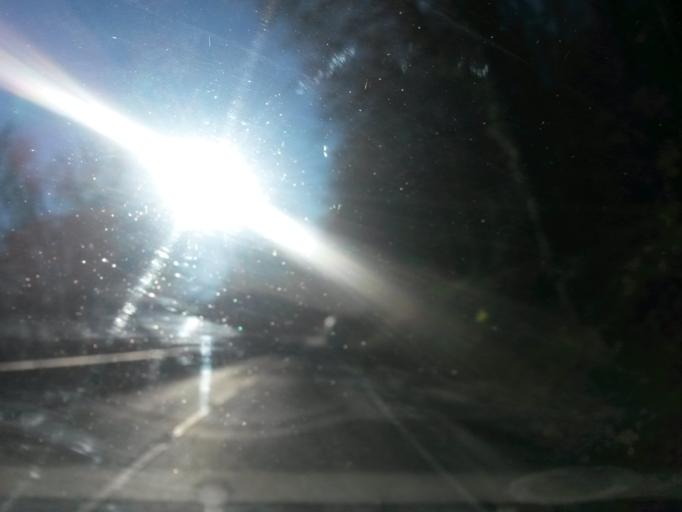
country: ES
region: Catalonia
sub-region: Provincia de Girona
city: Sant Feliu de Pallerols
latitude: 42.0498
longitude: 2.5099
